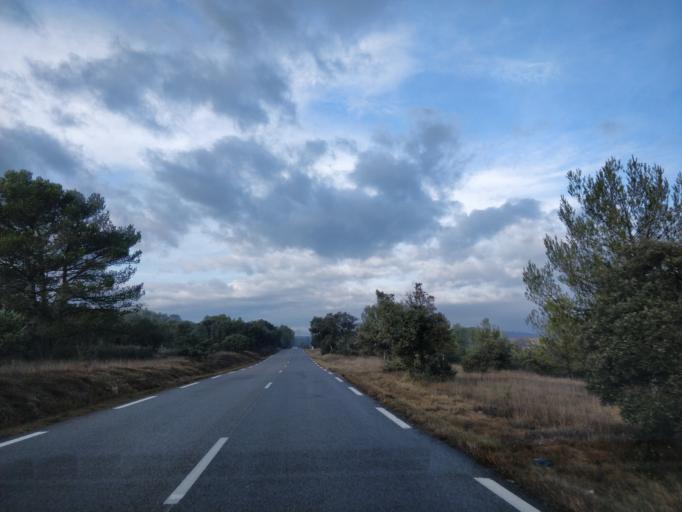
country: FR
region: Languedoc-Roussillon
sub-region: Departement du Gard
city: La Calmette
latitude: 43.8760
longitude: 4.2657
